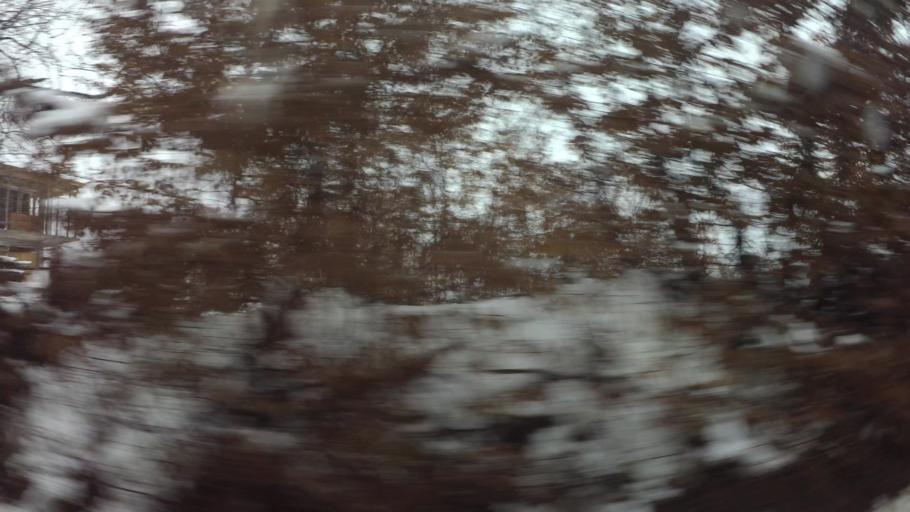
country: BA
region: Federation of Bosnia and Herzegovina
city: Hadzici
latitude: 43.8508
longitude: 18.2681
